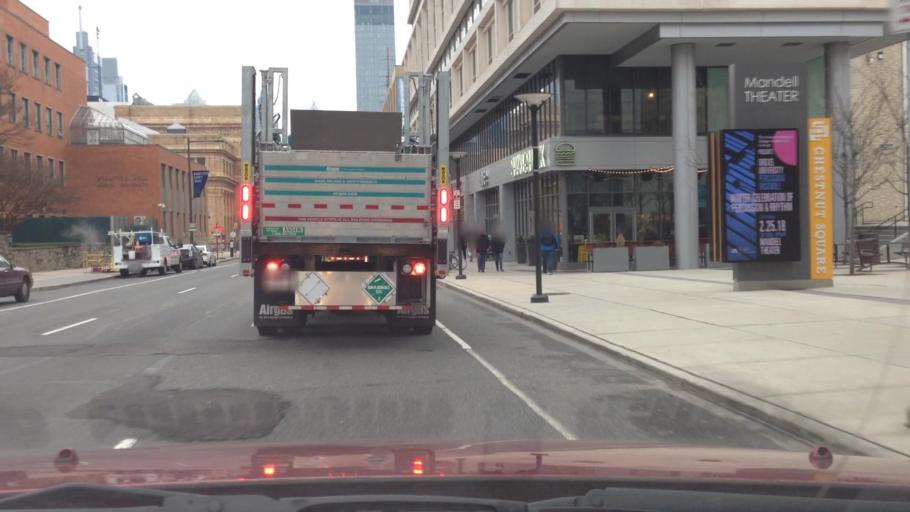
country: US
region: Pennsylvania
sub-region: Philadelphia County
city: Philadelphia
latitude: 39.9537
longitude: -75.1869
